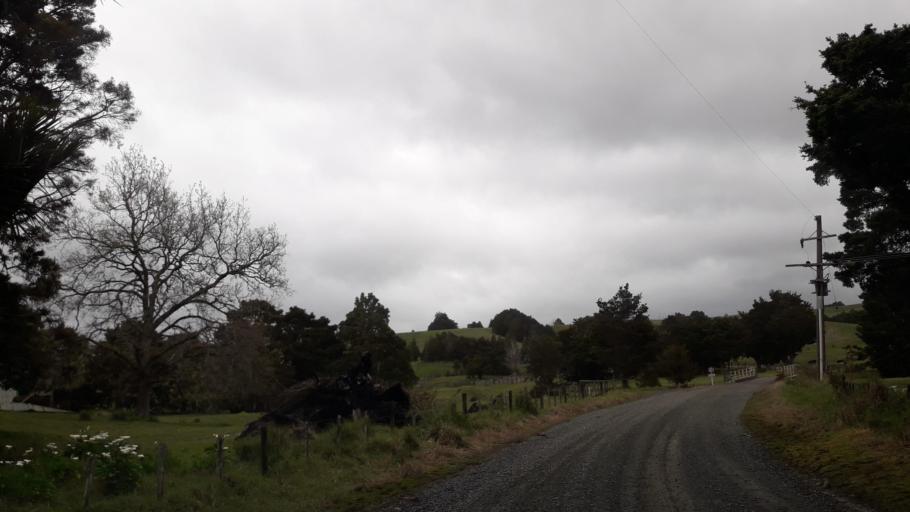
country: NZ
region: Northland
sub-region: Far North District
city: Waimate North
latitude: -35.1356
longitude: 173.7145
